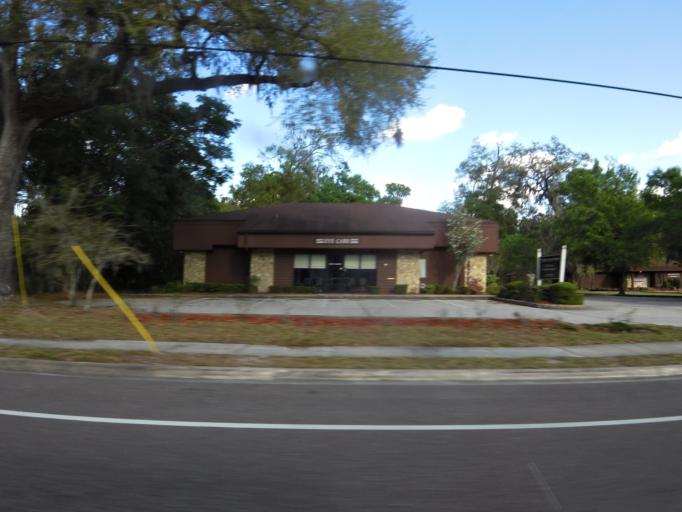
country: US
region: Florida
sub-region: Duval County
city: Jacksonville
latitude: 30.3310
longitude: -81.5969
